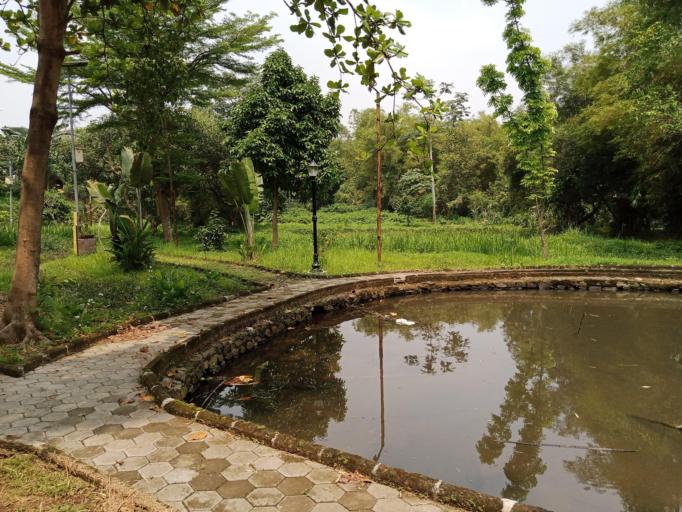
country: ID
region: West Java
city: Depok
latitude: -6.3948
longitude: 106.8094
